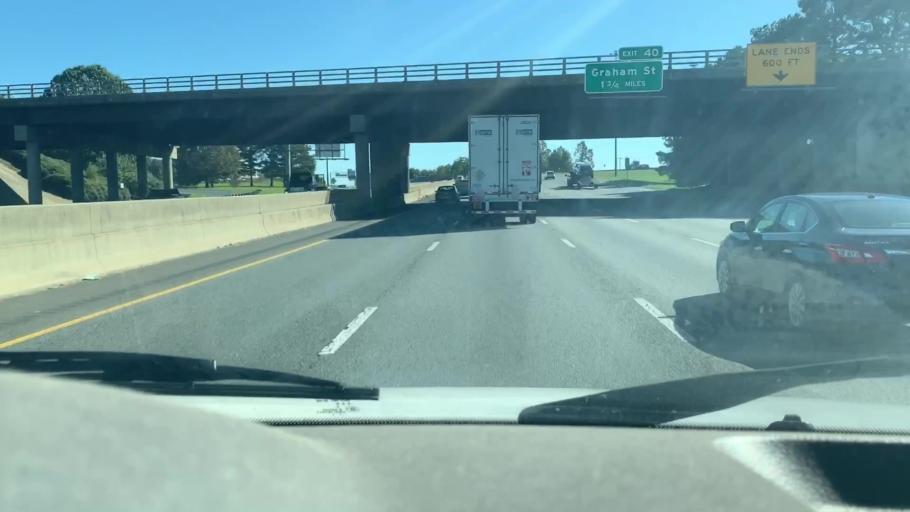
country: US
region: North Carolina
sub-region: Mecklenburg County
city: Charlotte
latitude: 35.2728
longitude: -80.8372
